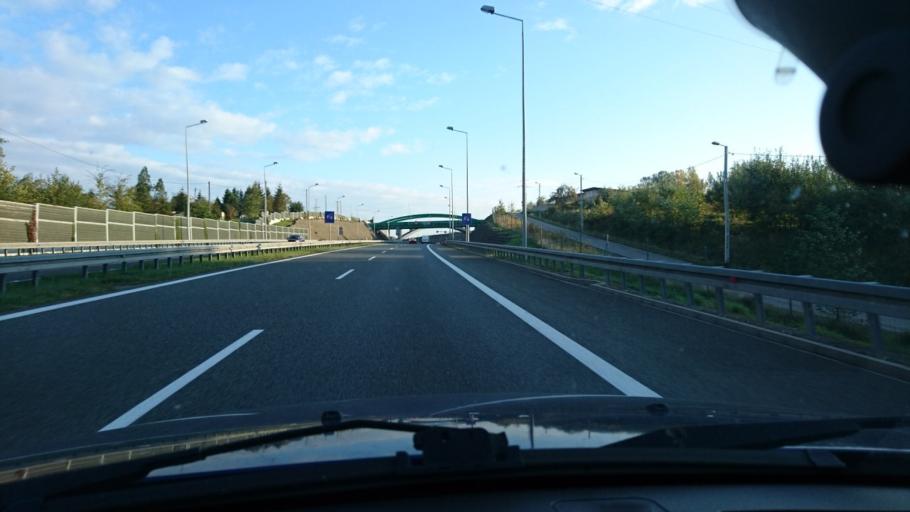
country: PL
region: Silesian Voivodeship
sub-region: Bielsko-Biala
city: Bielsko-Biala
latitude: 49.8391
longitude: 19.0880
